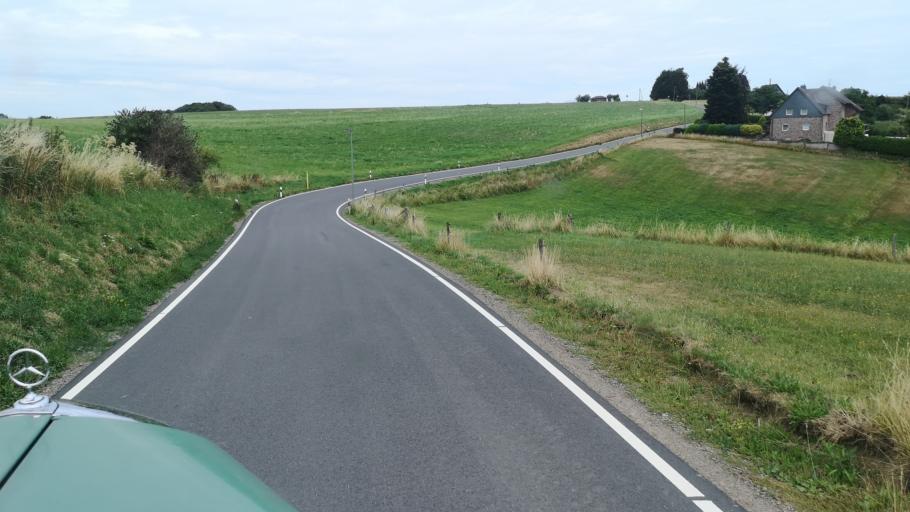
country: DE
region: North Rhine-Westphalia
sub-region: Regierungsbezirk Koln
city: Kurten
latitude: 51.0449
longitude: 7.2023
